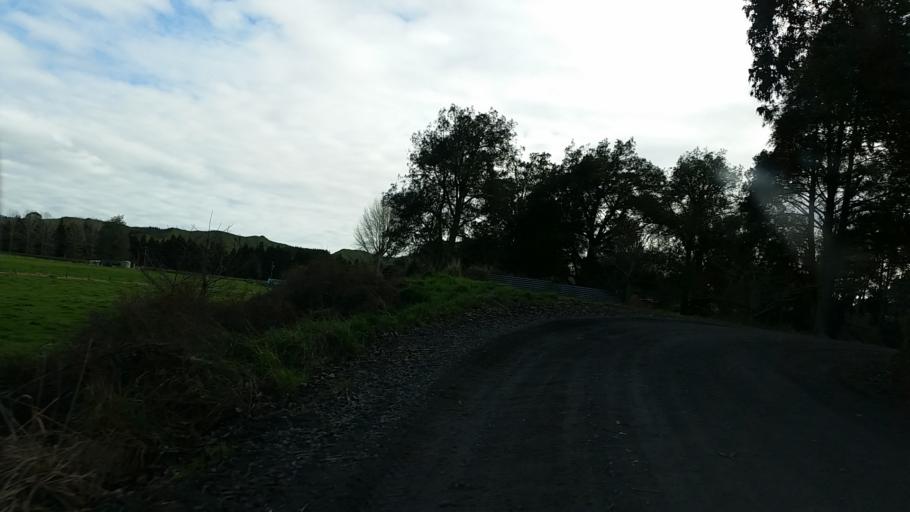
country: NZ
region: Taranaki
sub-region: South Taranaki District
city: Eltham
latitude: -39.2550
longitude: 174.5102
